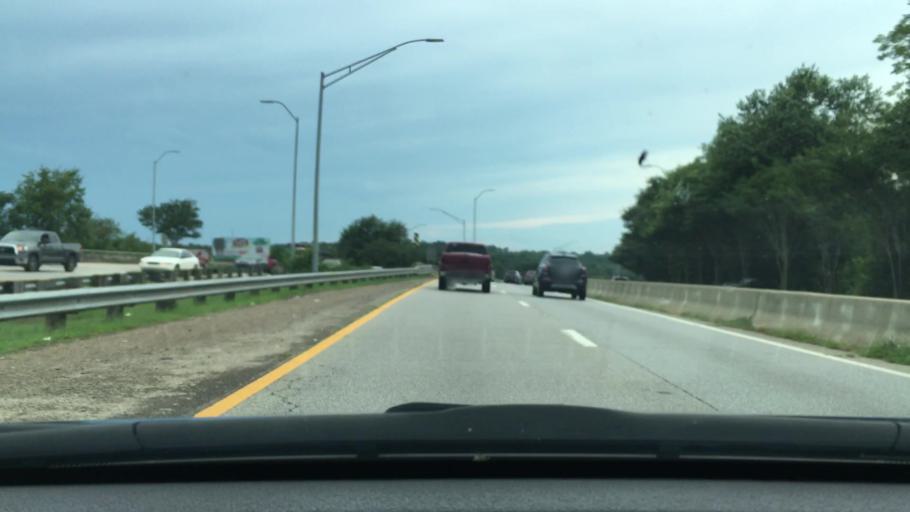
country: US
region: South Carolina
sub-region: Richland County
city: Columbia
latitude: 34.0087
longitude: -81.0537
